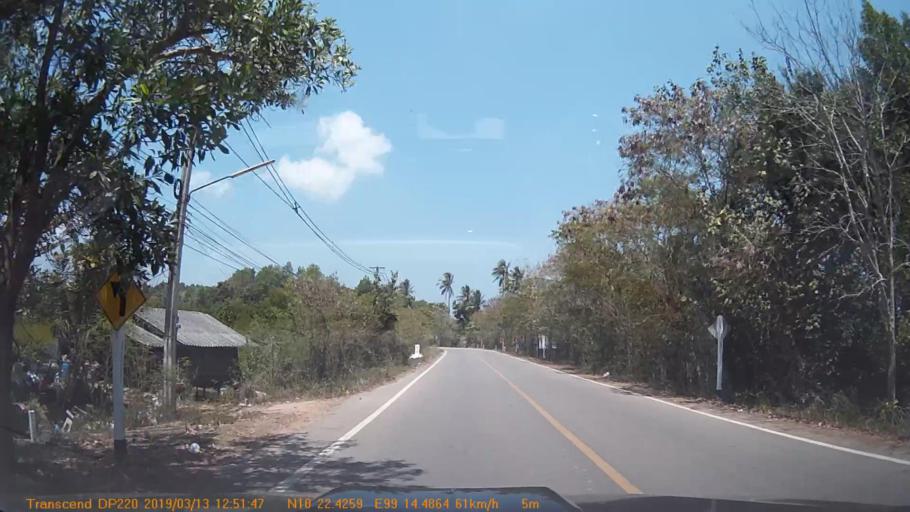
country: TH
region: Chumphon
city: Chumphon
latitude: 10.3741
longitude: 99.2415
